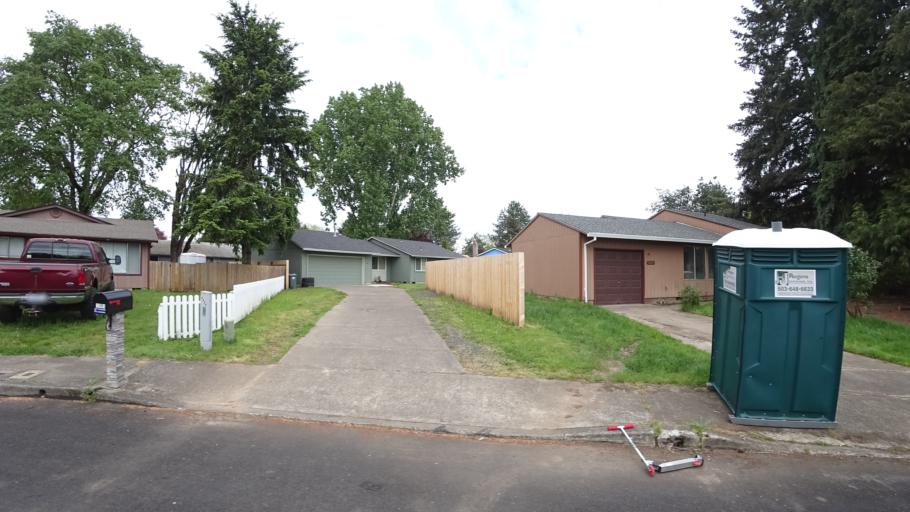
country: US
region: Oregon
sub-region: Washington County
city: Hillsboro
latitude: 45.4933
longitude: -122.9643
